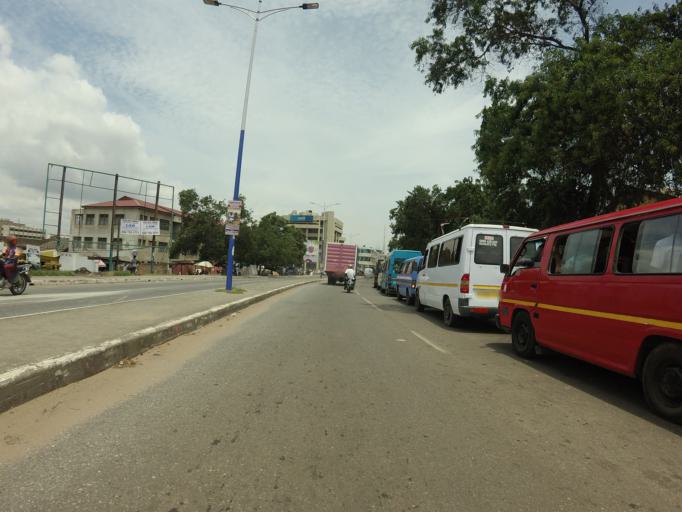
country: GH
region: Greater Accra
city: Accra
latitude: 5.5547
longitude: -0.2127
